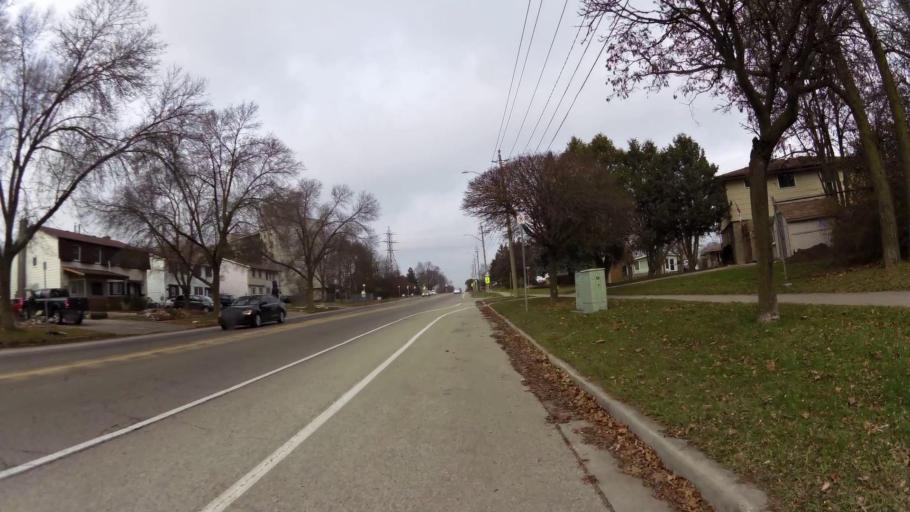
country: CA
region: Ontario
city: Kitchener
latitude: 43.4179
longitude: -80.4821
